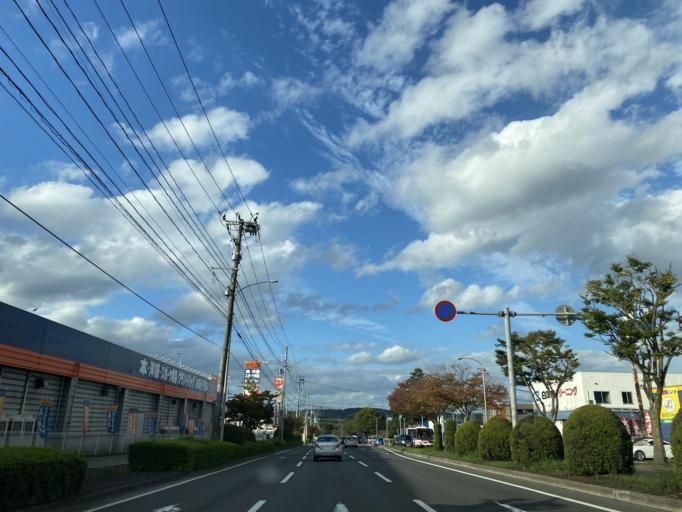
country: JP
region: Miyagi
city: Sendai-shi
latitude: 38.3185
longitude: 140.8445
